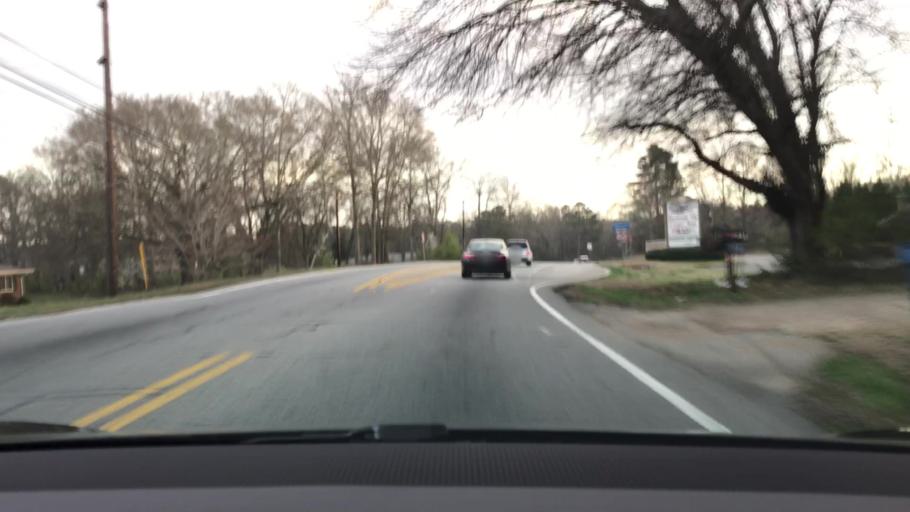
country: US
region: Georgia
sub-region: Barrow County
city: Russell
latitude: 33.9301
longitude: -83.7138
